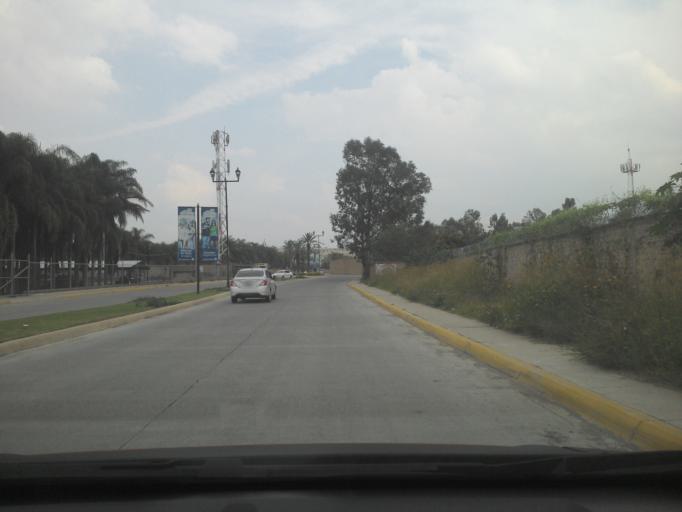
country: MX
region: Jalisco
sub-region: Tlajomulco de Zuniga
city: Lomas de San Agustin
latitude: 20.5299
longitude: -103.4678
